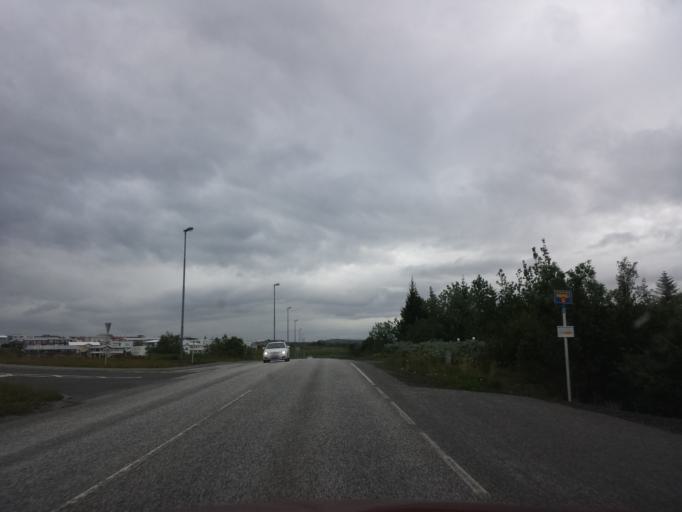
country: IS
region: Capital Region
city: Hafnarfjoerdur
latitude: 64.0847
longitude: -21.9583
